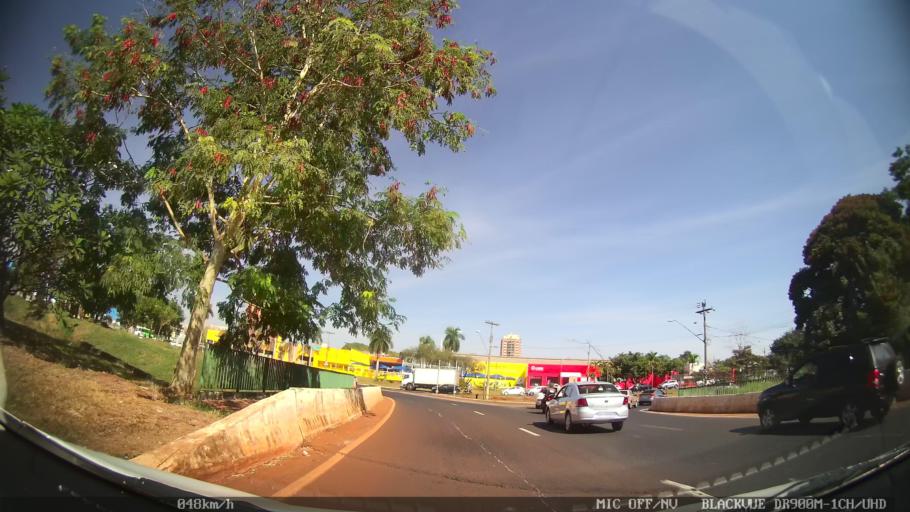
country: BR
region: Sao Paulo
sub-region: Ribeirao Preto
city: Ribeirao Preto
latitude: -21.1660
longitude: -47.8153
